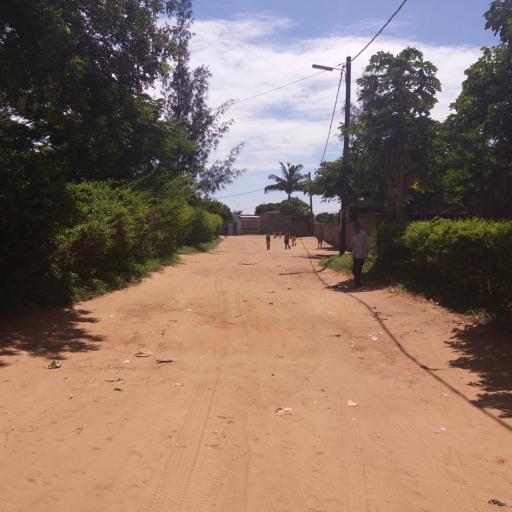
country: MZ
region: Maputo City
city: Maputo
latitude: -25.9057
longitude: 32.5903
